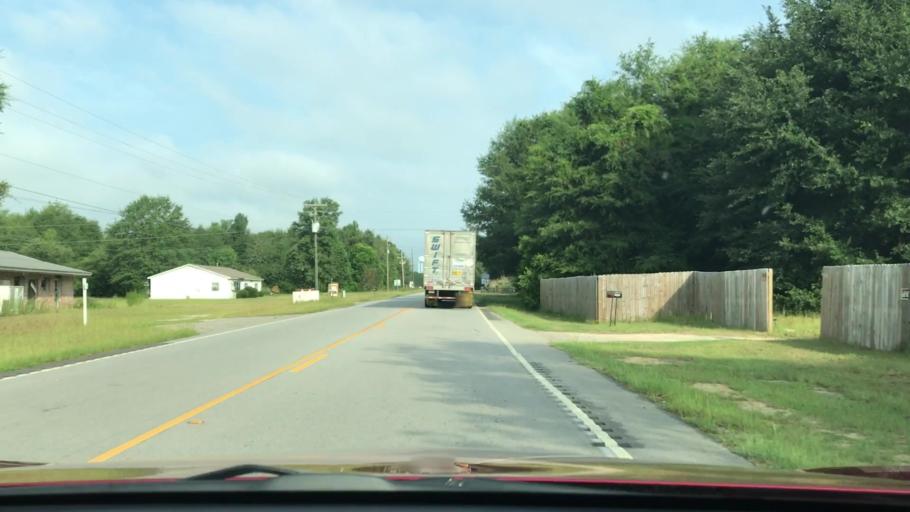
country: US
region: South Carolina
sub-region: Barnwell County
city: Williston
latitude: 33.6349
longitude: -81.3190
